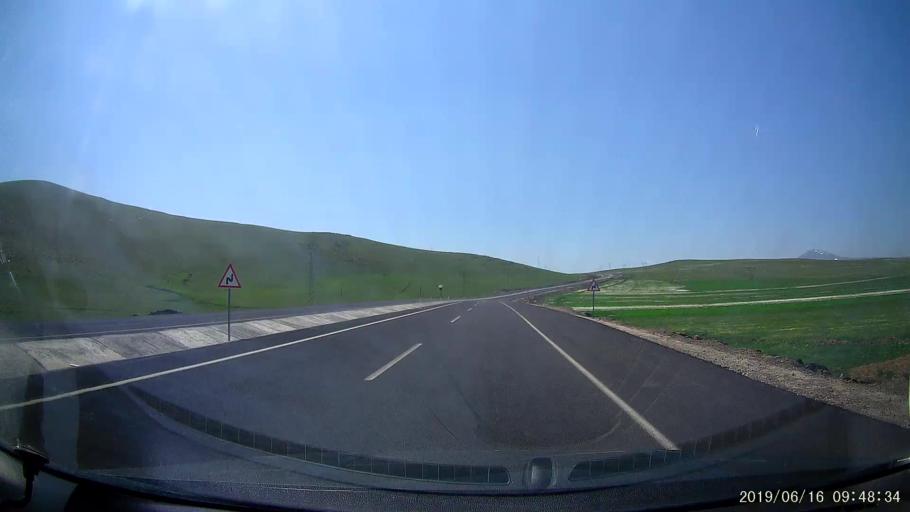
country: TR
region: Kars
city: Digor
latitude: 40.4321
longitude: 43.3541
